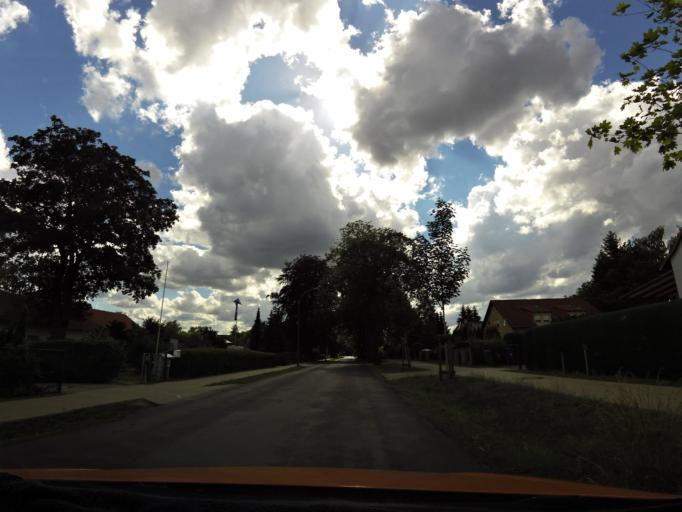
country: DE
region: Brandenburg
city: Konigs Wusterhausen
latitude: 52.2973
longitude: 13.6135
